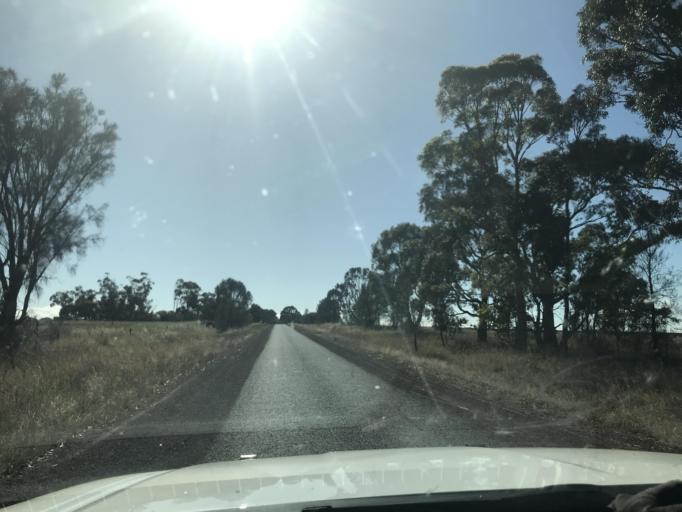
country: AU
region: Victoria
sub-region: Horsham
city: Horsham
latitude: -37.0063
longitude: 141.6337
